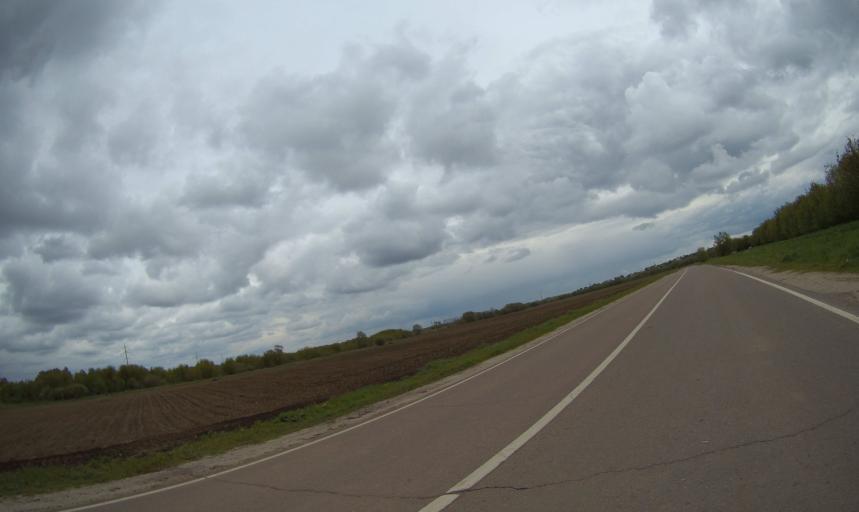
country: RU
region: Moskovskaya
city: Raduzhnyy
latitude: 55.1155
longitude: 38.7590
